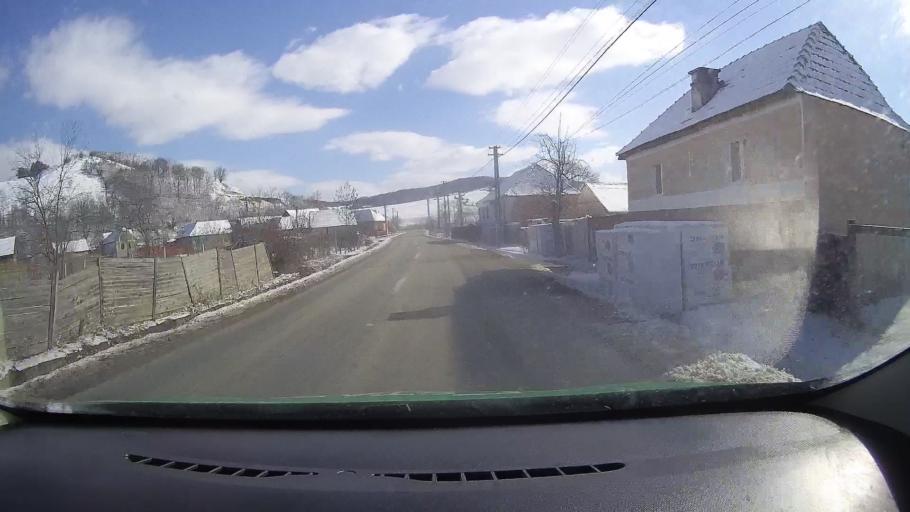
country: RO
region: Sibiu
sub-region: Comuna Barghis
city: Barghis
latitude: 45.9864
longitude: 24.4867
